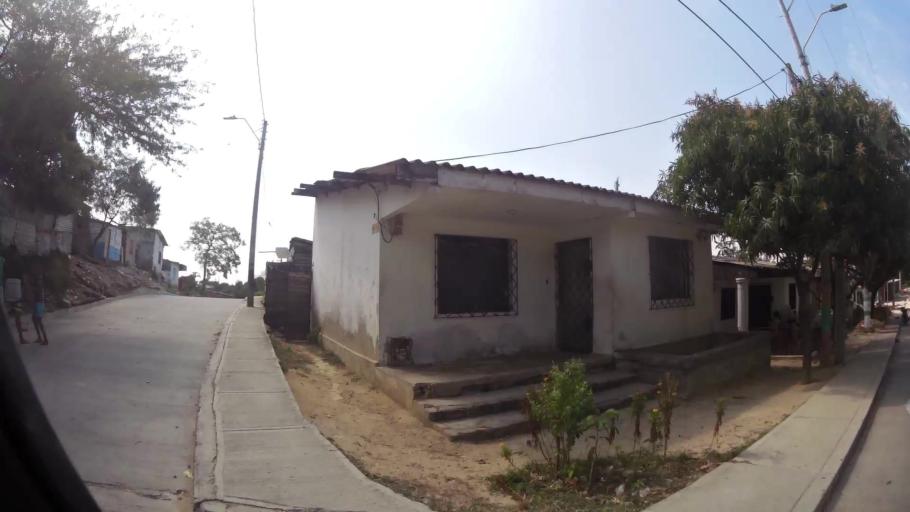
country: CO
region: Atlantico
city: Barranquilla
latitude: 10.9666
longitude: -74.8265
